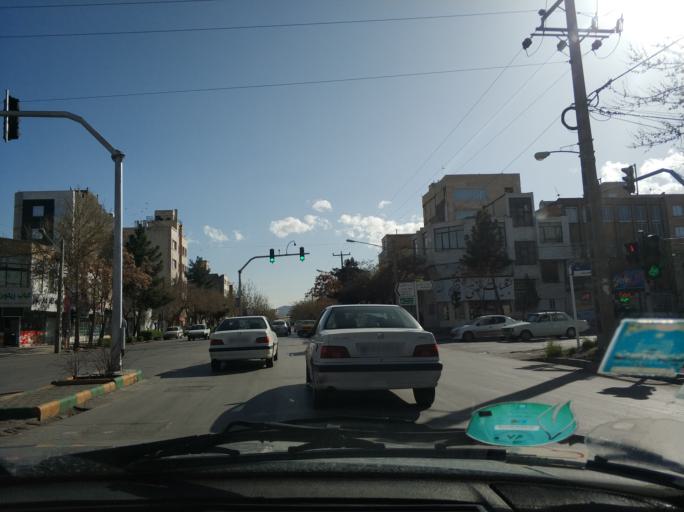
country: IR
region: Razavi Khorasan
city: Mashhad
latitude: 36.3146
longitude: 59.6263
